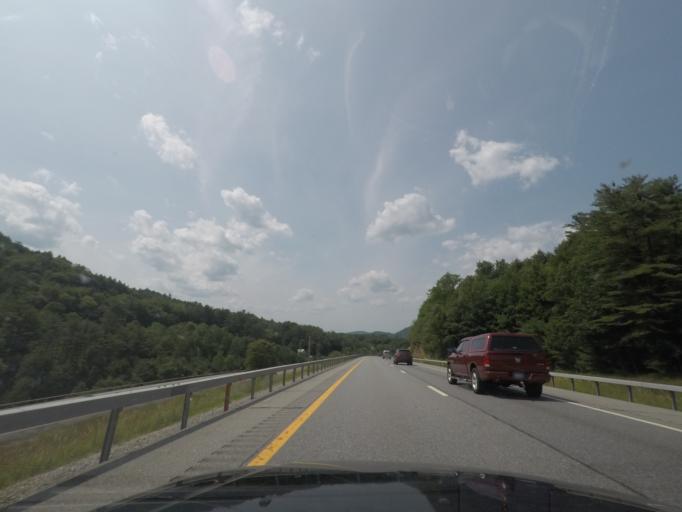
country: US
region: New York
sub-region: Warren County
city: Warrensburg
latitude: 43.4767
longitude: -73.7520
